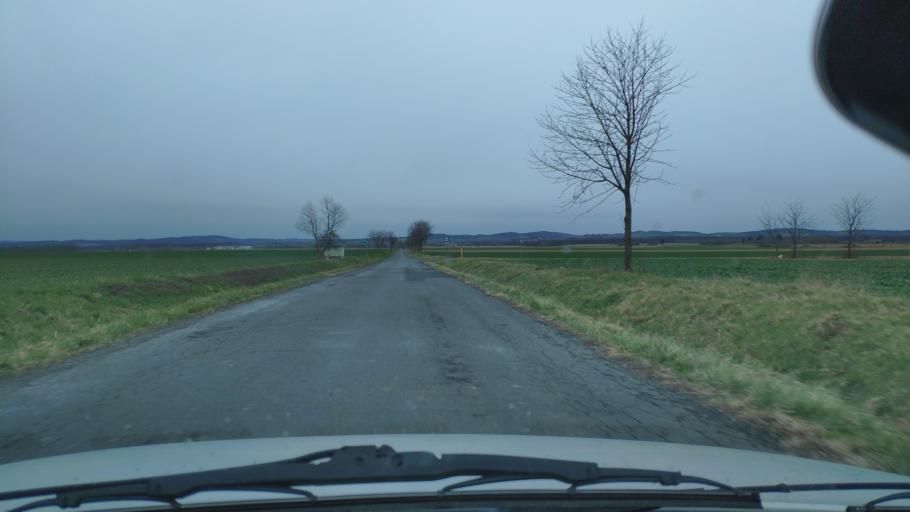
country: HU
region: Zala
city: Pacsa
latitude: 46.7079
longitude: 17.0425
